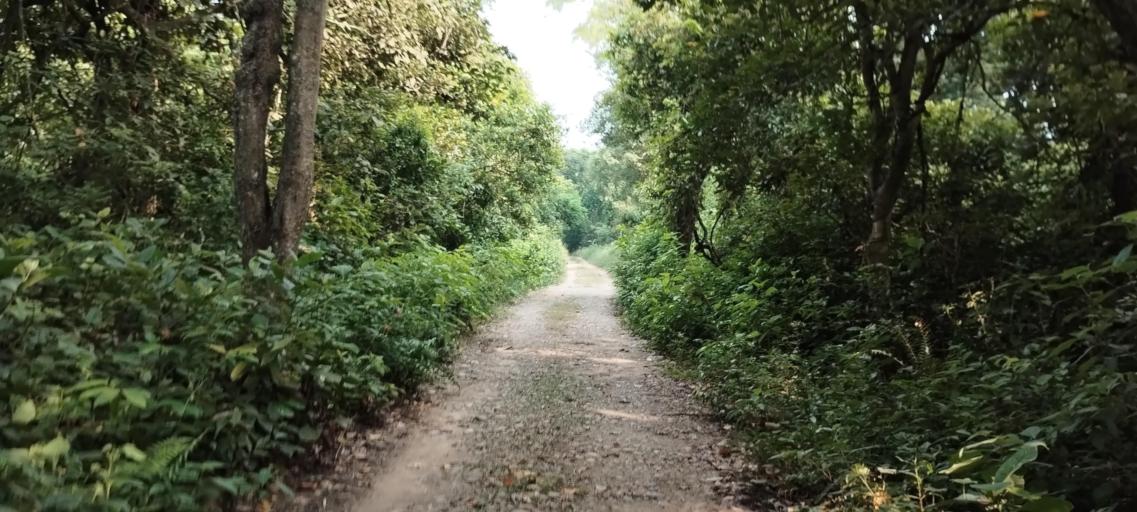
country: NP
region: Far Western
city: Tikapur
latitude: 28.4598
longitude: 81.2417
